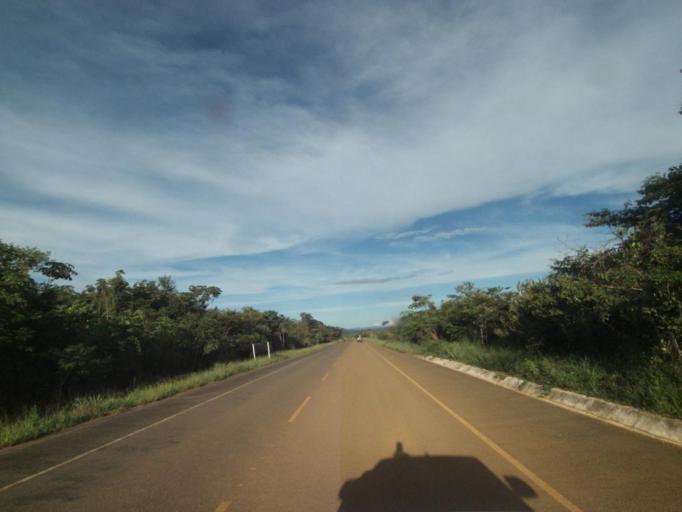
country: BR
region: Goias
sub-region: Jaragua
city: Jaragua
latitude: -15.8870
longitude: -49.4566
